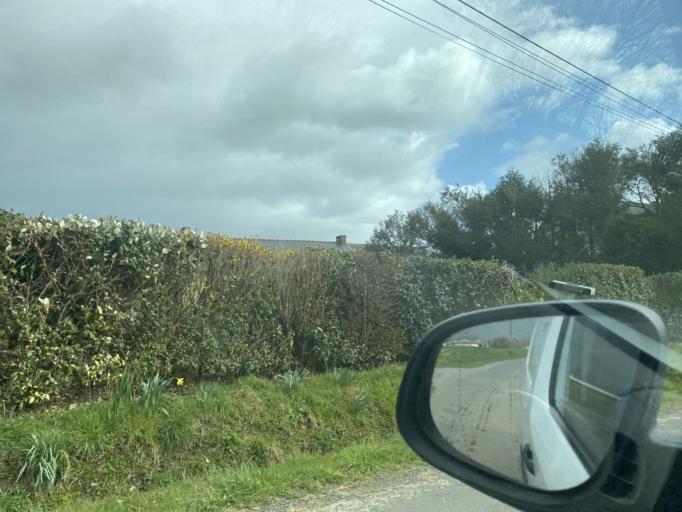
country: FR
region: Brittany
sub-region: Departement d'Ille-et-Vilaine
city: Melesse
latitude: 48.1868
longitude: -1.7004
